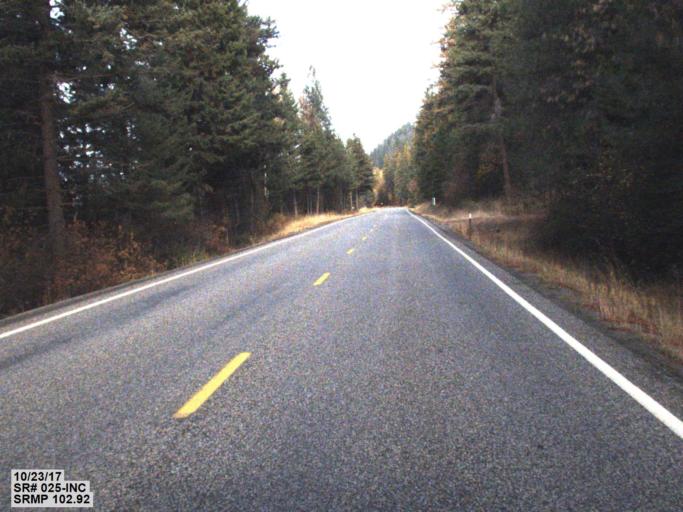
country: US
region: Washington
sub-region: Stevens County
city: Kettle Falls
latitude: 48.8162
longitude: -117.9264
